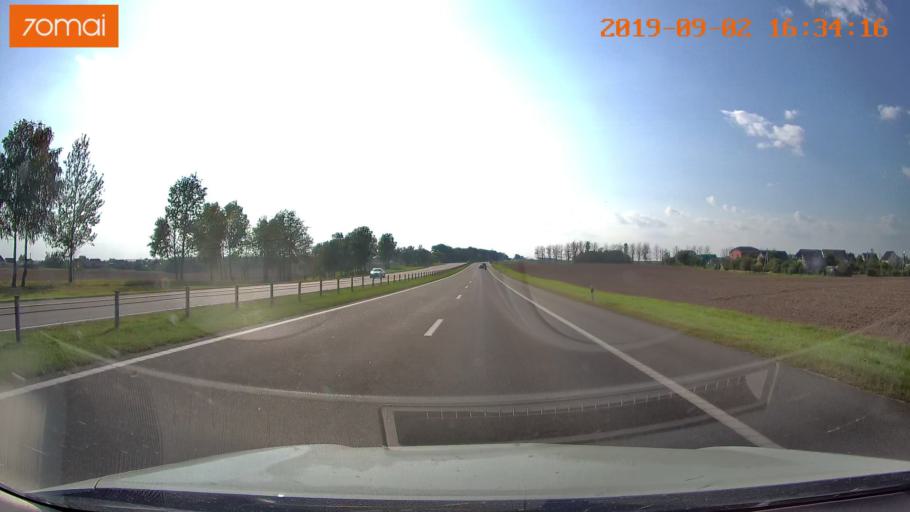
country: BY
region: Minsk
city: Smilavichy
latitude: 53.7596
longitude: 28.0405
